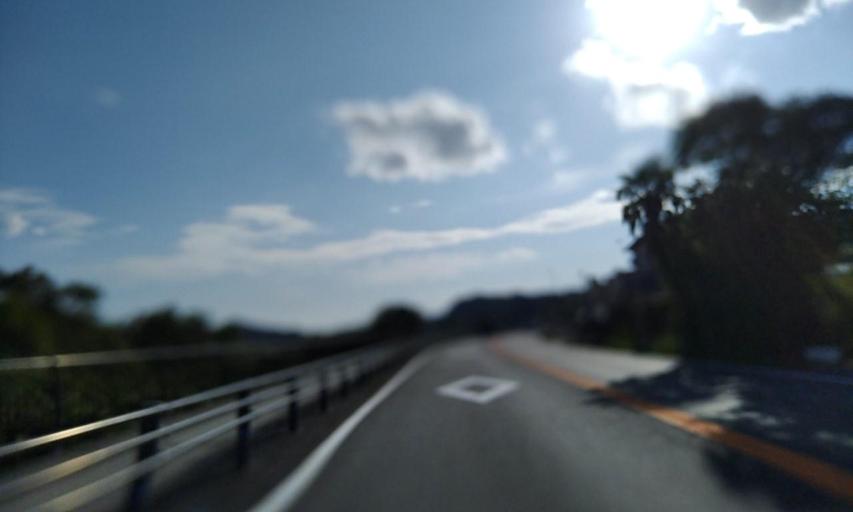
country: JP
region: Wakayama
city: Tanabe
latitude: 33.6836
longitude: 135.4111
